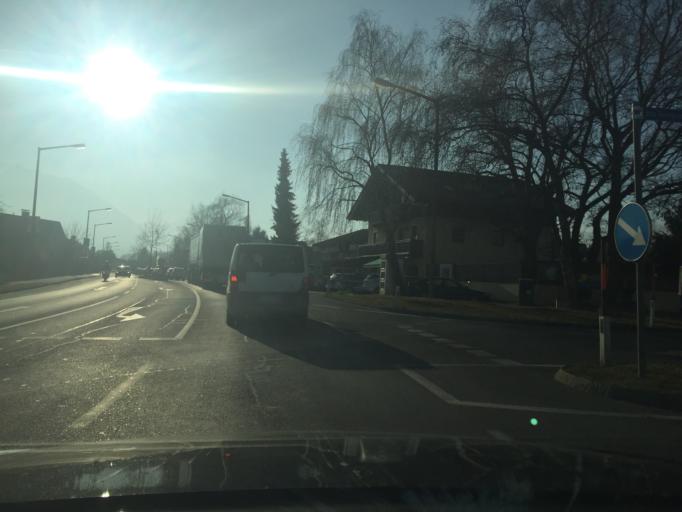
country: DE
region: Bavaria
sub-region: Upper Bavaria
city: Ainring
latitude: 47.7899
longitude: 12.9867
